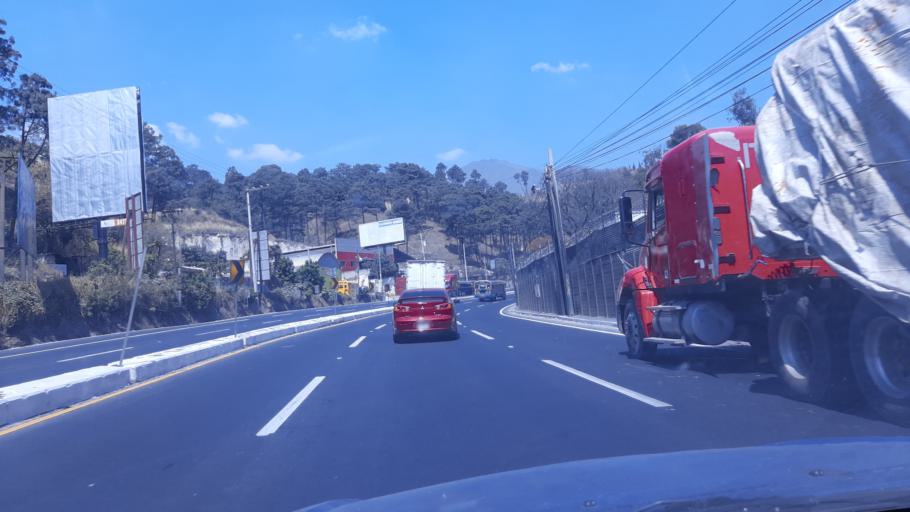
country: GT
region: Guatemala
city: Amatitlan
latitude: 14.4935
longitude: -90.6277
